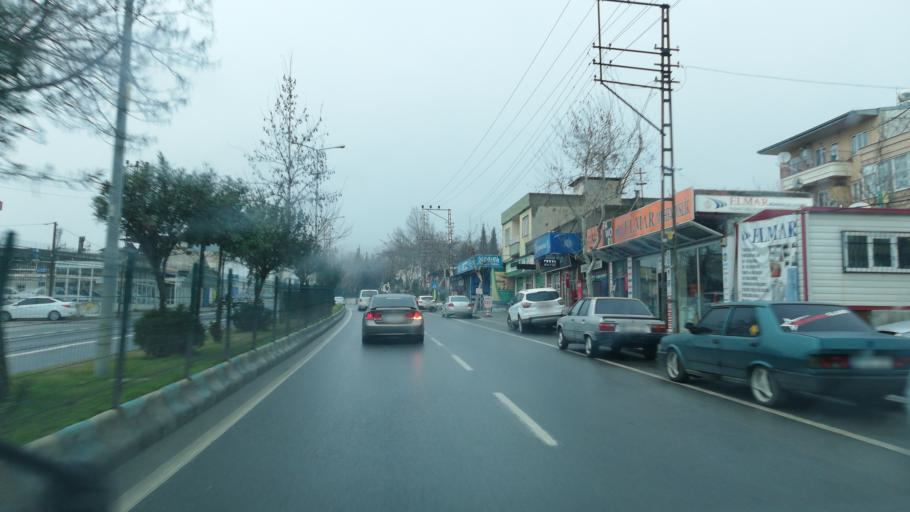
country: TR
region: Kahramanmaras
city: Kahramanmaras
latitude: 37.5696
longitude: 36.9463
